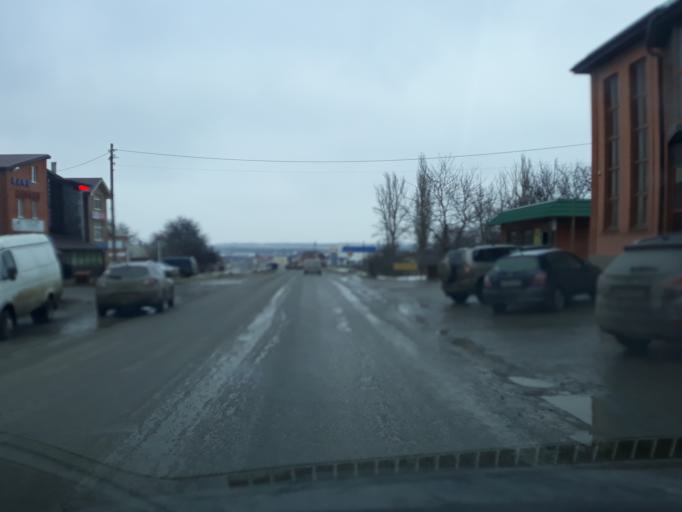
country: RU
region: Rostov
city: Krym
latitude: 47.2783
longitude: 39.5131
